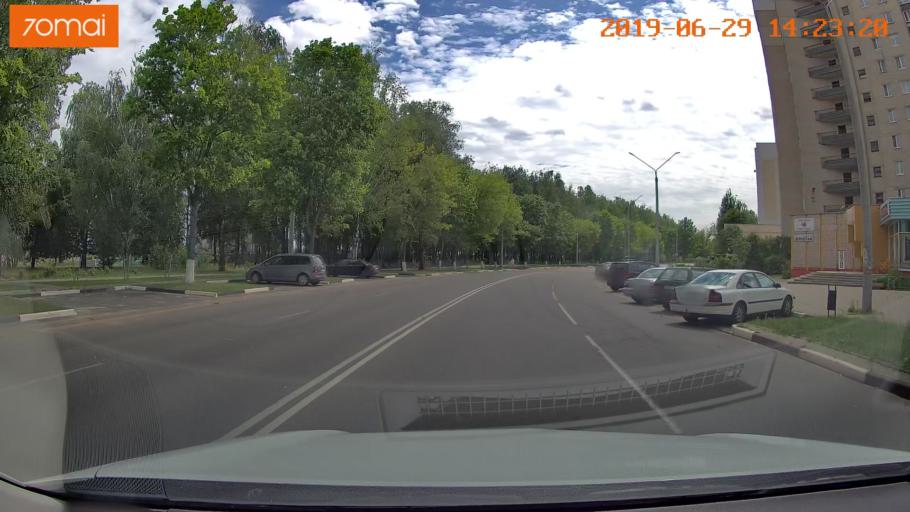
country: BY
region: Minsk
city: Salihorsk
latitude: 52.7864
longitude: 27.5544
